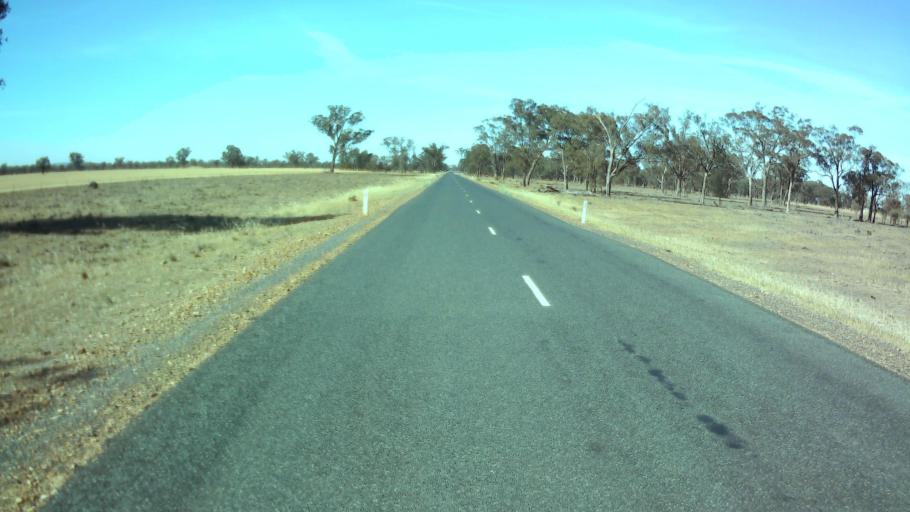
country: AU
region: New South Wales
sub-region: Weddin
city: Grenfell
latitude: -34.0870
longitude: 147.8917
